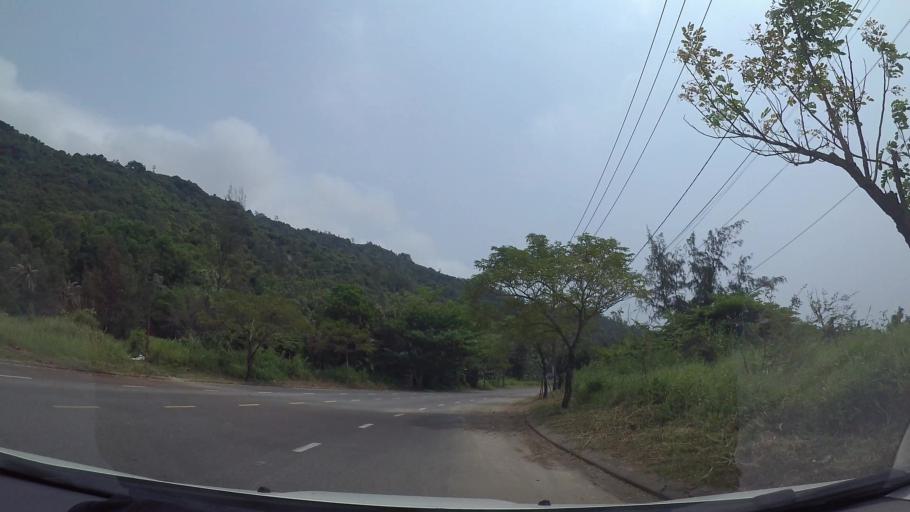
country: VN
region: Da Nang
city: Son Tra
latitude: 16.1077
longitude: 108.2621
